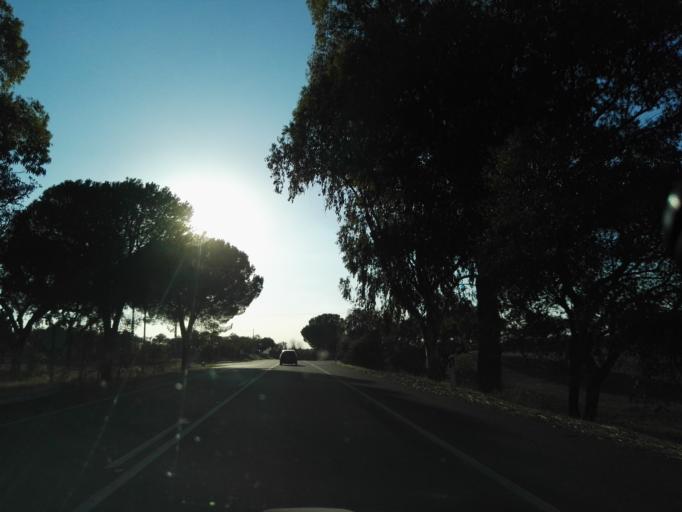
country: PT
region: Evora
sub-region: Estremoz
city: Estremoz
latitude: 38.8244
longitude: -7.7726
